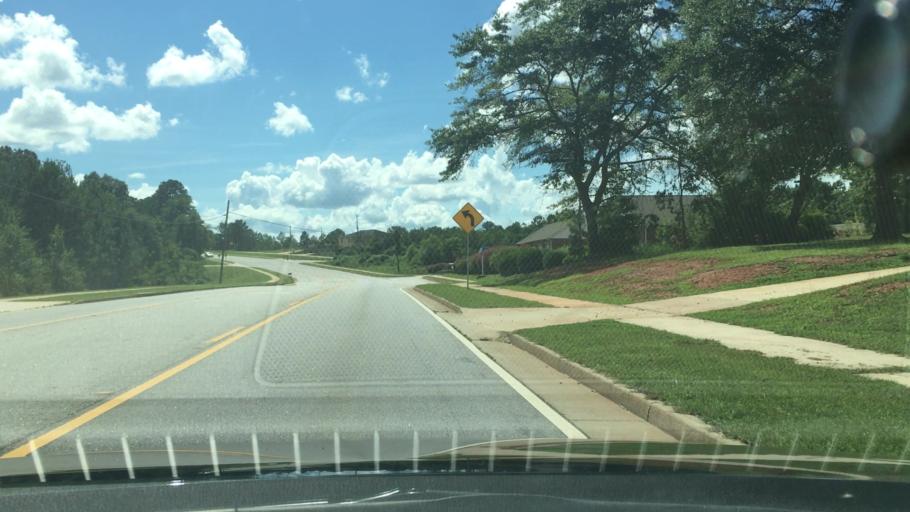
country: US
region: Georgia
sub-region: Jasper County
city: Monticello
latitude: 33.3055
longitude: -83.6978
